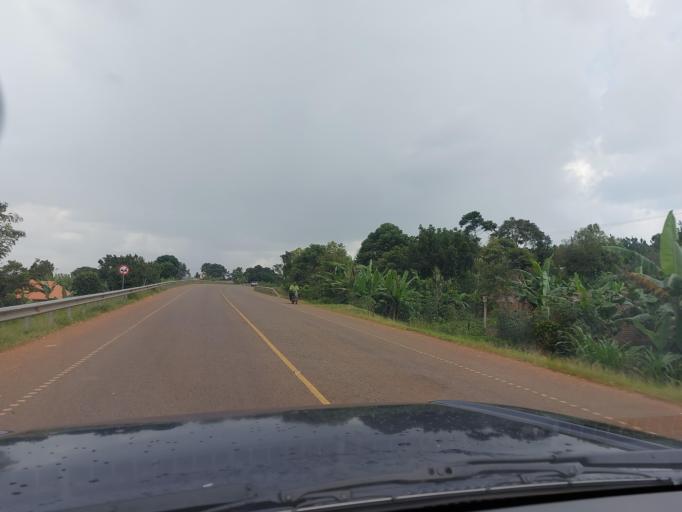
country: UG
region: Central Region
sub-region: Buikwe District
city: Buikwe
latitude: 0.2403
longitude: 32.9294
